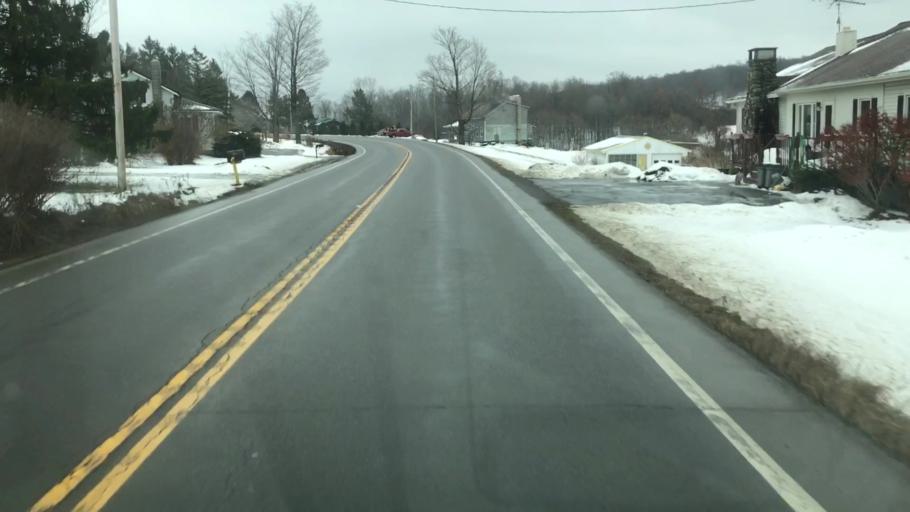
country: US
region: New York
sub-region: Cortland County
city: Cortland West
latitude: 42.6439
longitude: -76.2448
